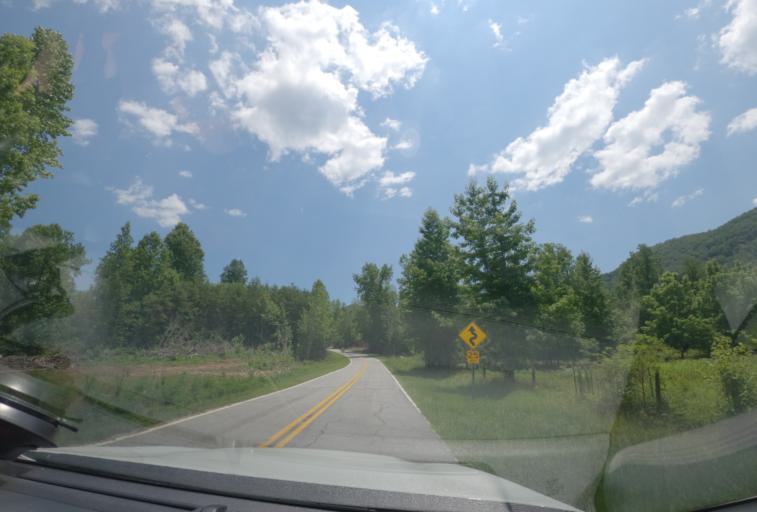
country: US
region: South Carolina
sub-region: Pickens County
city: Pickens
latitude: 34.9961
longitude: -82.8273
